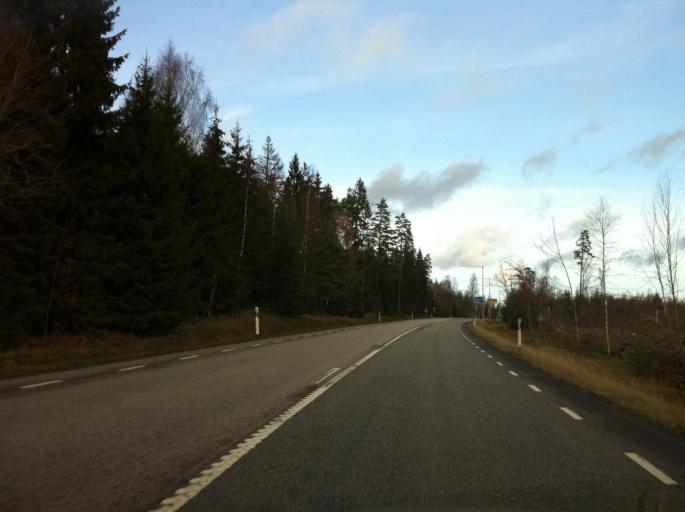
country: SE
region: Kronoberg
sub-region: Almhults Kommun
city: AElmhult
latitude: 56.5616
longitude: 14.1820
